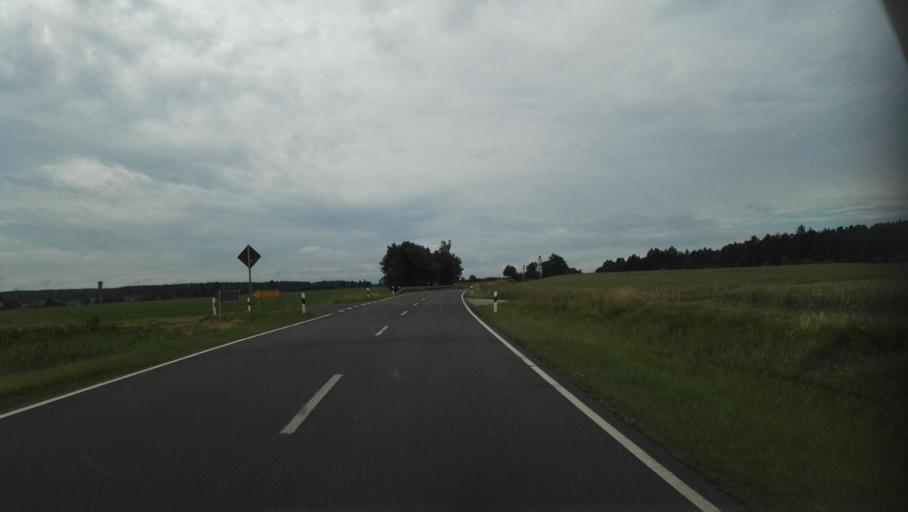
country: DE
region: Bavaria
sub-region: Upper Franconia
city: Hollfeld
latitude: 49.9130
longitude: 11.3148
